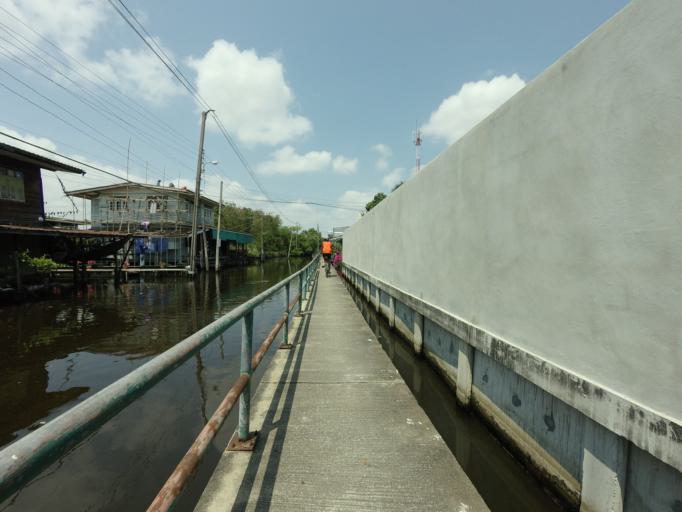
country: TH
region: Bangkok
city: Chom Thong
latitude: 13.6523
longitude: 100.4716
